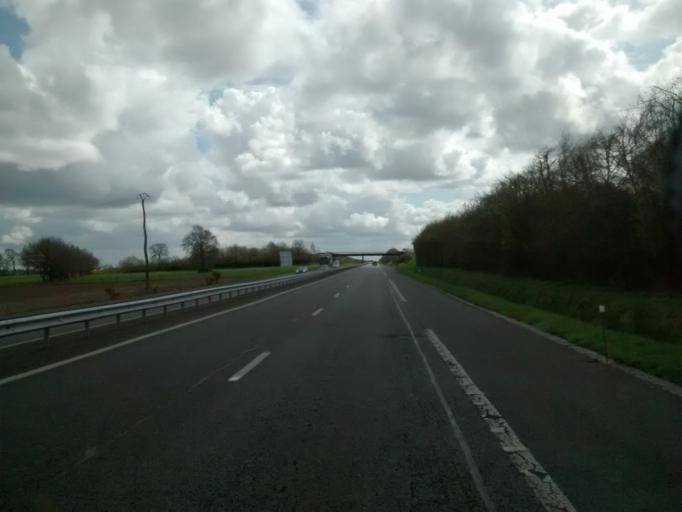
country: FR
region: Brittany
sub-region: Departement d'Ille-et-Vilaine
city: Plelan-le-Grand
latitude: 47.9915
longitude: -2.0980
